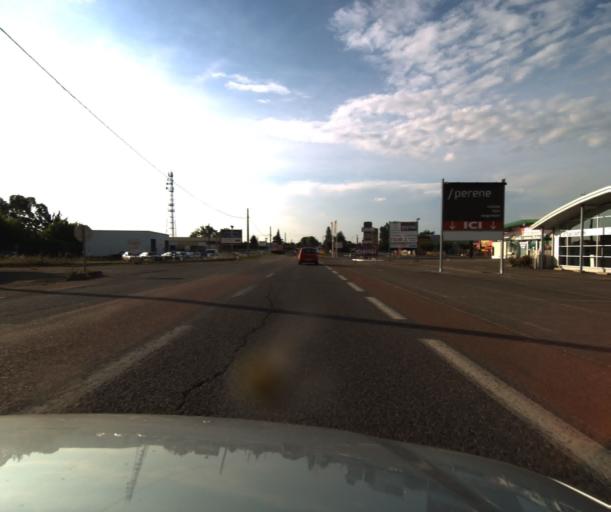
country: FR
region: Midi-Pyrenees
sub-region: Departement du Tarn-et-Garonne
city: Castelsarrasin
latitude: 44.0611
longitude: 1.0981
